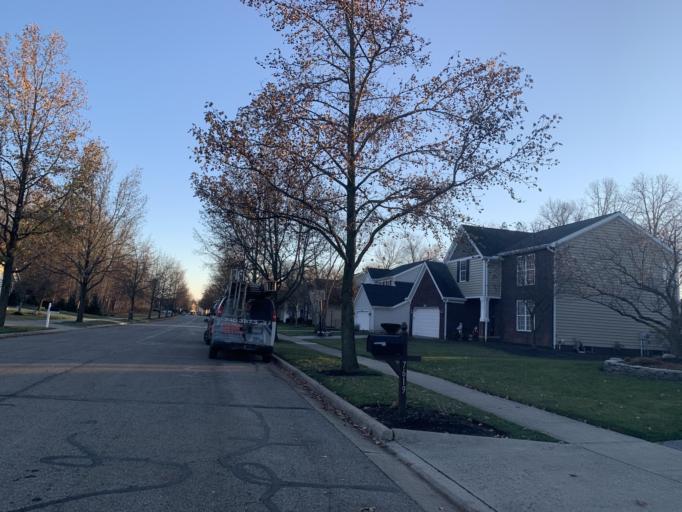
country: US
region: Ohio
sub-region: Franklin County
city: Dublin
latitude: 40.1239
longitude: -83.1636
